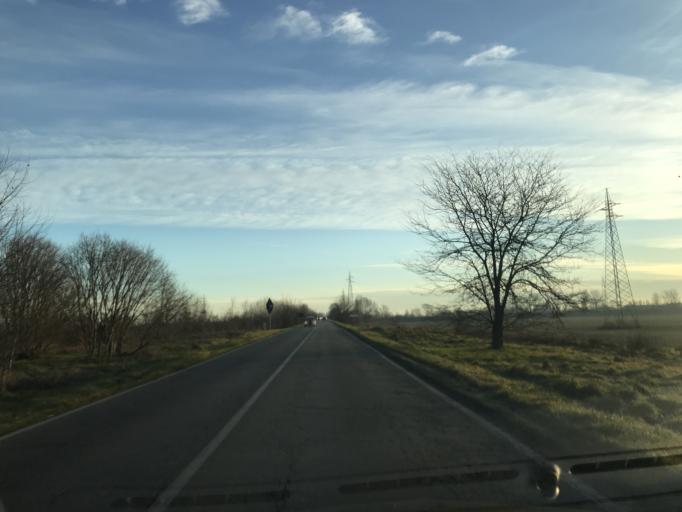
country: IT
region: Lombardy
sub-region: Provincia di Lodi
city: Salerano sul Lambro
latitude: 45.3018
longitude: 9.3855
